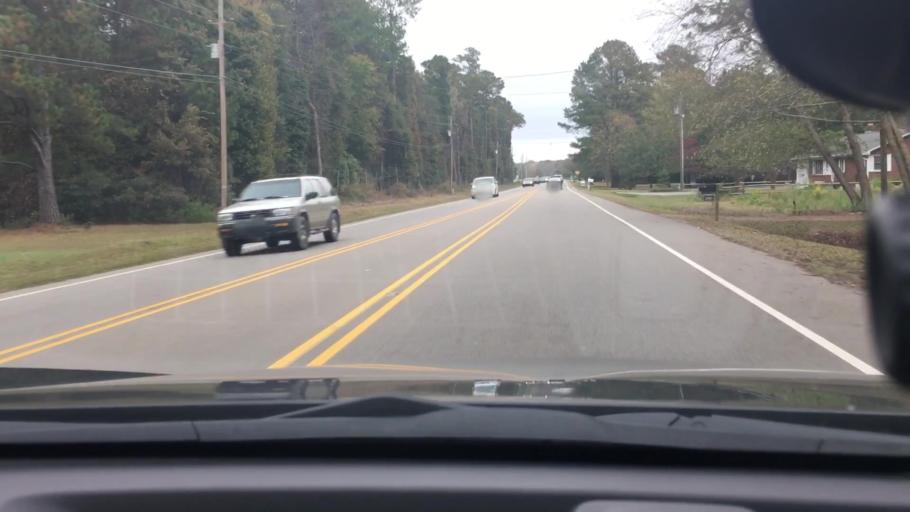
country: US
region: North Carolina
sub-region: Pitt County
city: Summerfield
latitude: 35.5828
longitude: -77.4171
